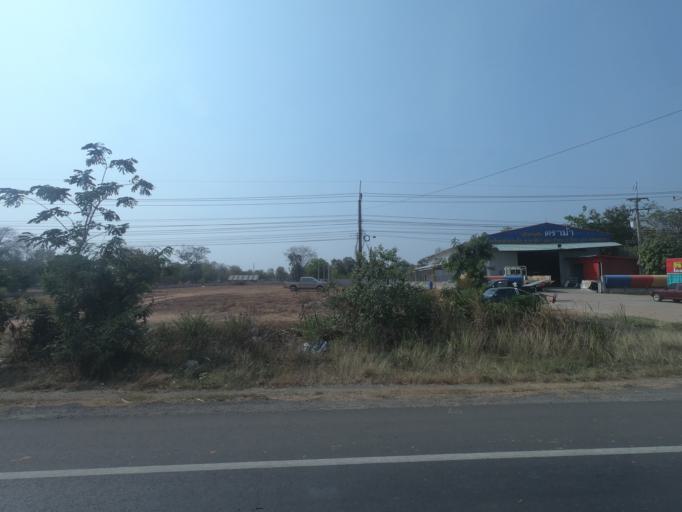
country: TH
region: Nakhon Ratchasima
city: Sida
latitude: 15.5853
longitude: 102.5572
